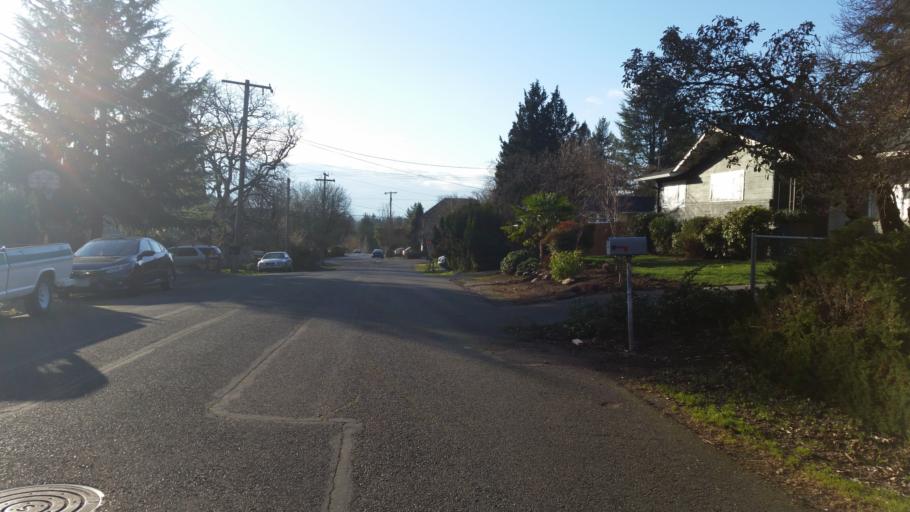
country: US
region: Oregon
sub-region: Washington County
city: Raleigh Hills
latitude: 45.4813
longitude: -122.7219
